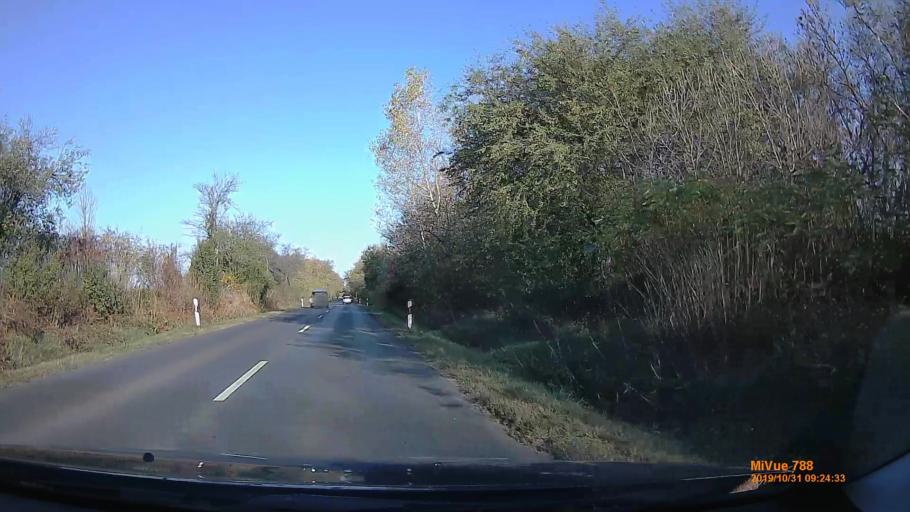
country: HU
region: Pest
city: Maglod
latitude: 47.4347
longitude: 19.3778
